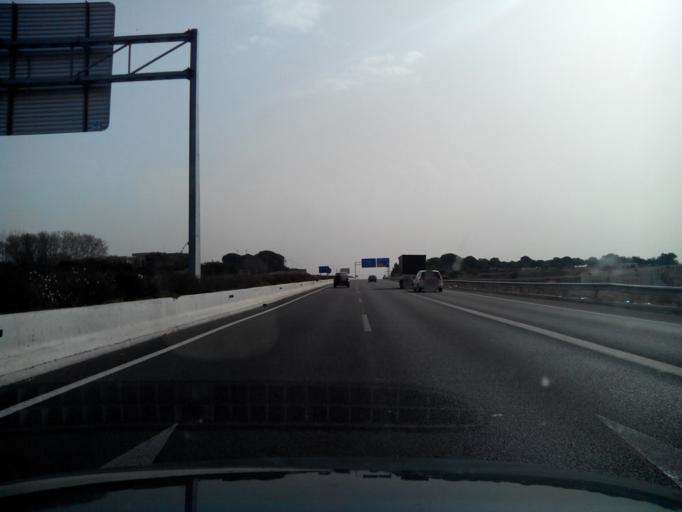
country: ES
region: Catalonia
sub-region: Provincia de Tarragona
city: Constanti
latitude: 41.1329
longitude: 1.1847
